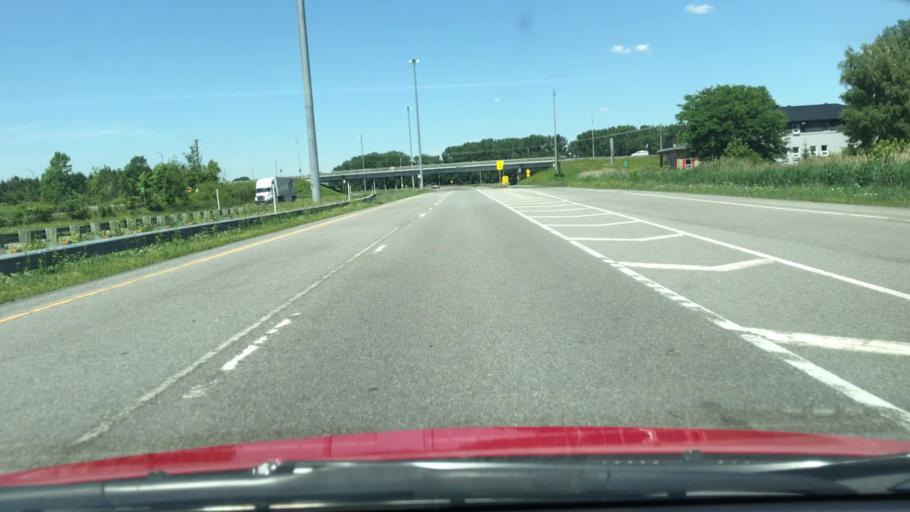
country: US
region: New York
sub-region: Clinton County
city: Champlain
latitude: 45.0656
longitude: -73.4543
